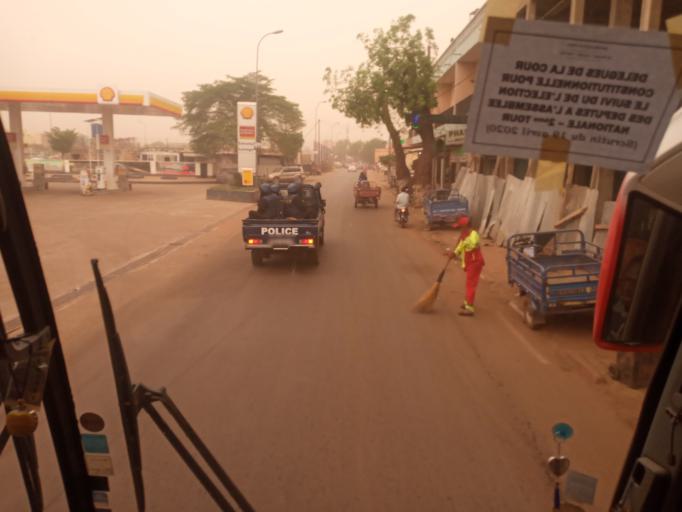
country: ML
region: Bamako
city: Bamako
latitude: 12.6516
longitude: -7.9906
